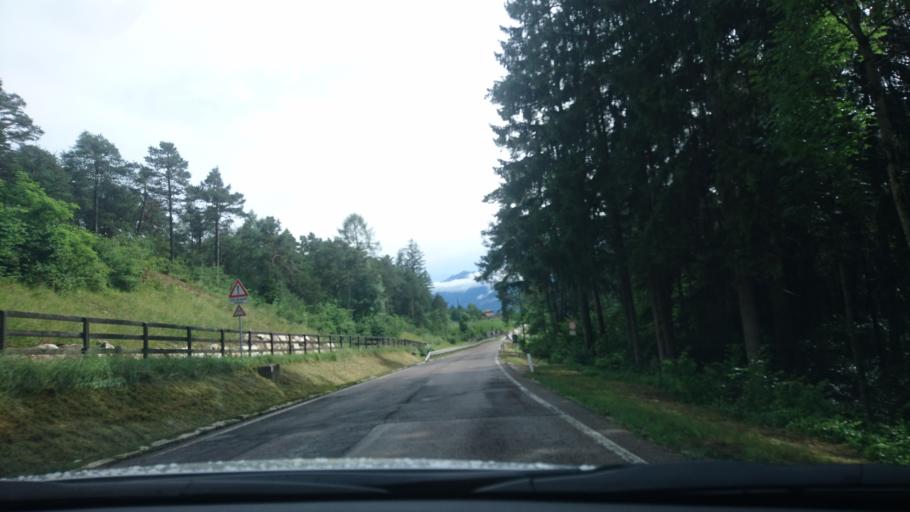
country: IT
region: Trentino-Alto Adige
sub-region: Provincia di Trento
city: Dambel
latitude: 46.3865
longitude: 11.0971
